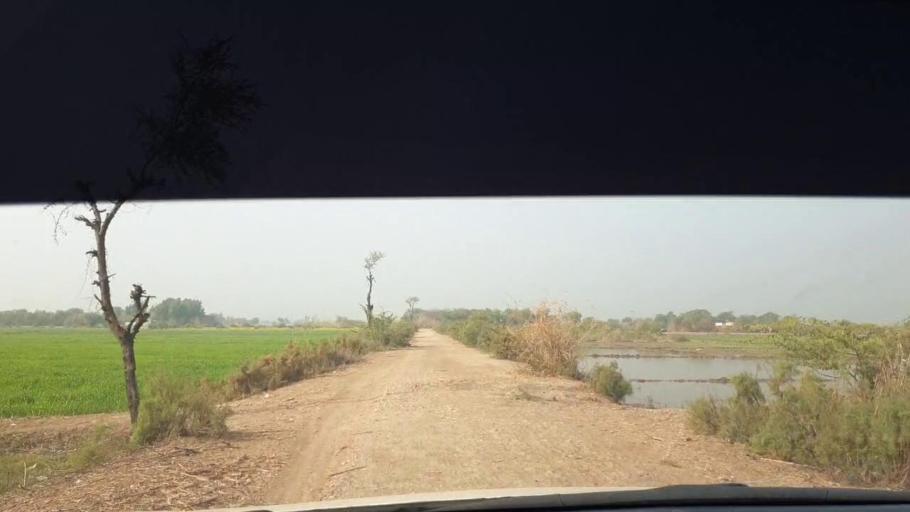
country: PK
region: Sindh
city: Berani
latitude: 25.7749
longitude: 68.8029
